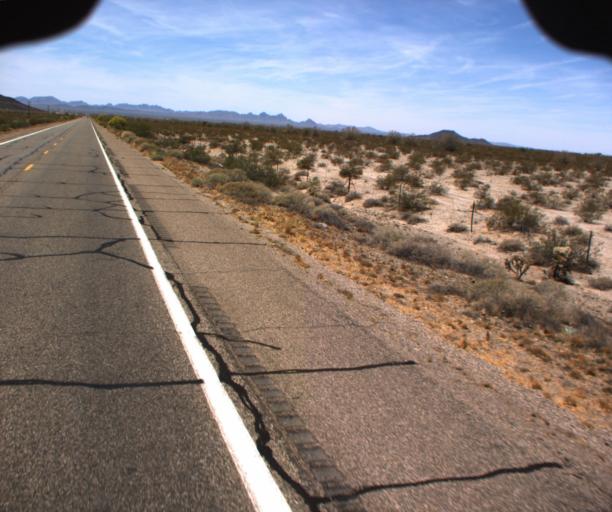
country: US
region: Arizona
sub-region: La Paz County
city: Salome
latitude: 33.7219
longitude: -113.7234
